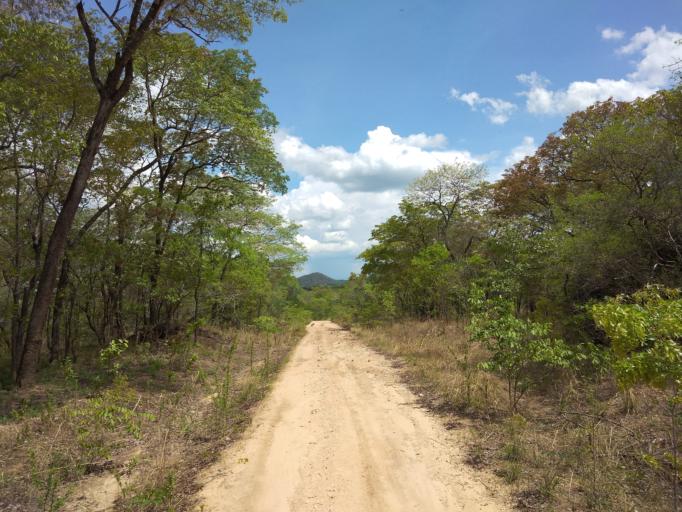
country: ZM
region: Central
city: Mkushi
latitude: -14.1318
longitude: 30.0471
